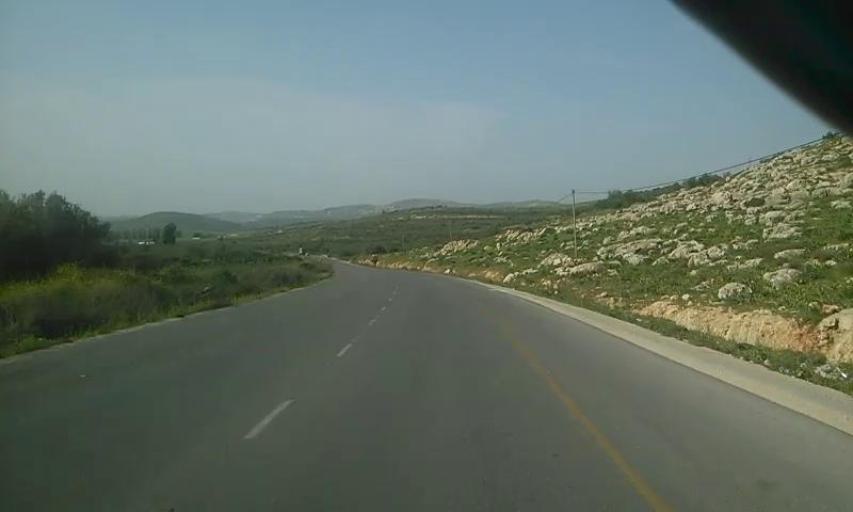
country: PS
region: West Bank
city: Dayr Sharaf
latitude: 32.2568
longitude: 35.1773
